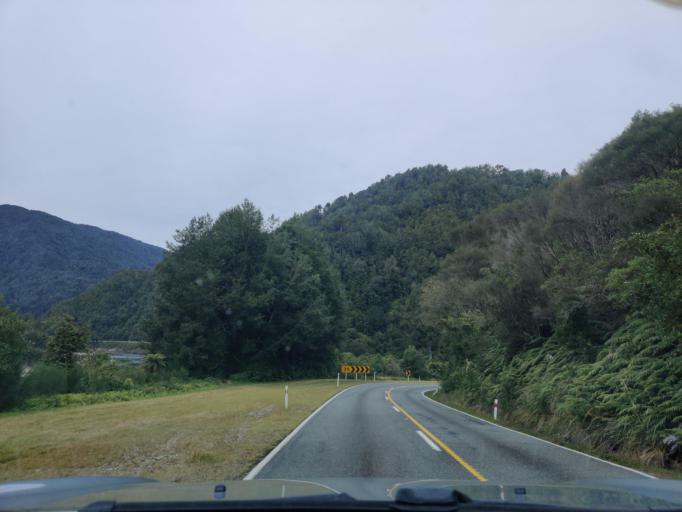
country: NZ
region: West Coast
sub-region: Buller District
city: Westport
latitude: -41.8489
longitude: 171.7288
